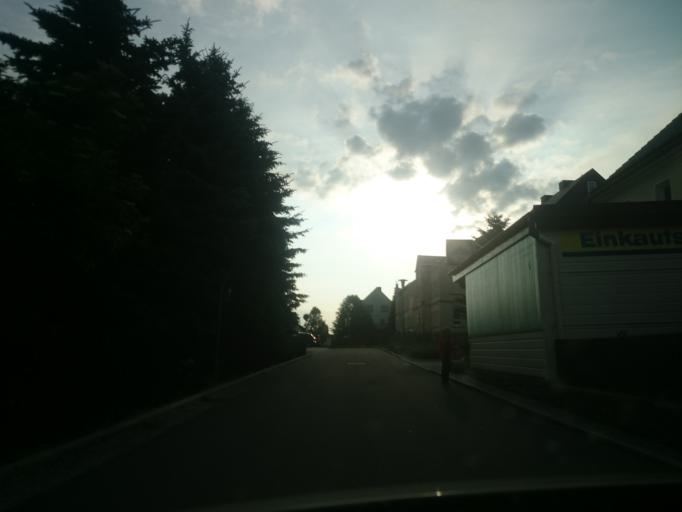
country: DE
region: Saxony
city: Bornichen
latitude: 50.7500
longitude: 13.1422
